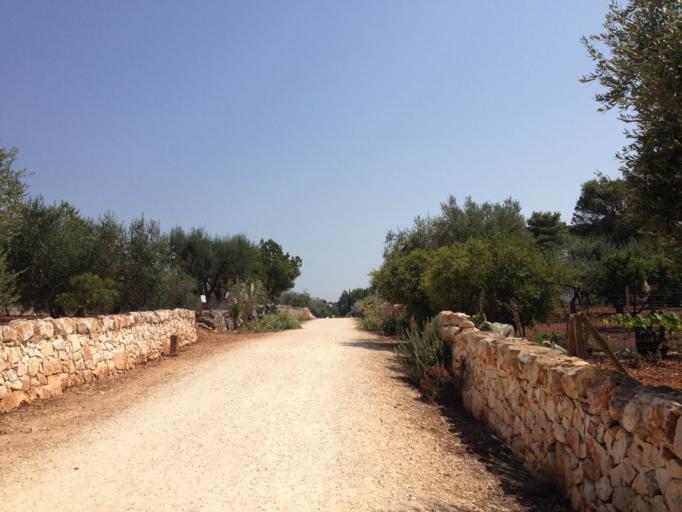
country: IT
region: Apulia
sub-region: Provincia di Brindisi
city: Cisternino
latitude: 40.7203
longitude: 17.4001
